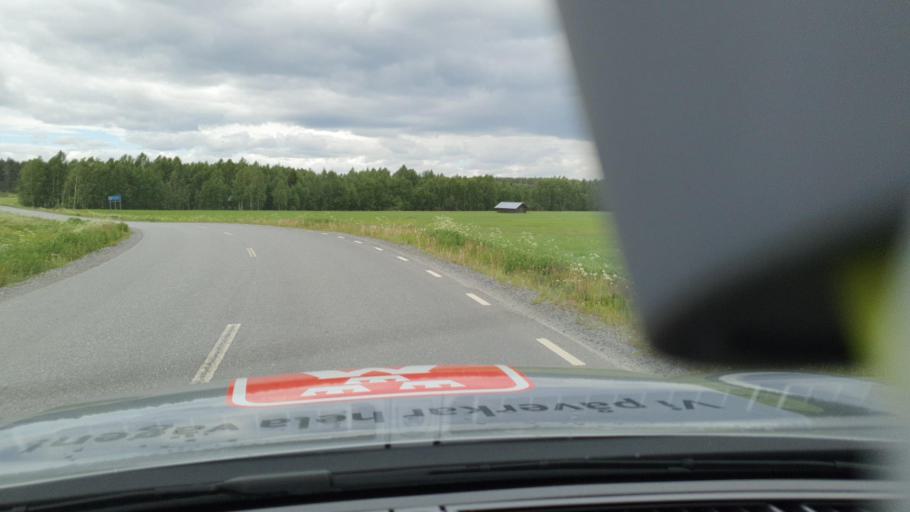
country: SE
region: Norrbotten
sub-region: Lulea Kommun
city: Sodra Sunderbyn
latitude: 65.8211
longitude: 21.9951
